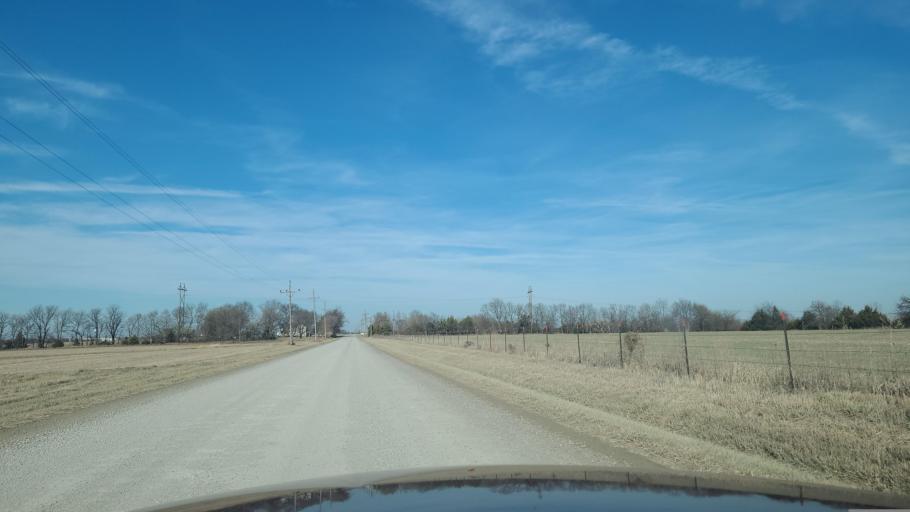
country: US
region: Kansas
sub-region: Douglas County
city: Eudora
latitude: 38.9181
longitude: -95.0748
